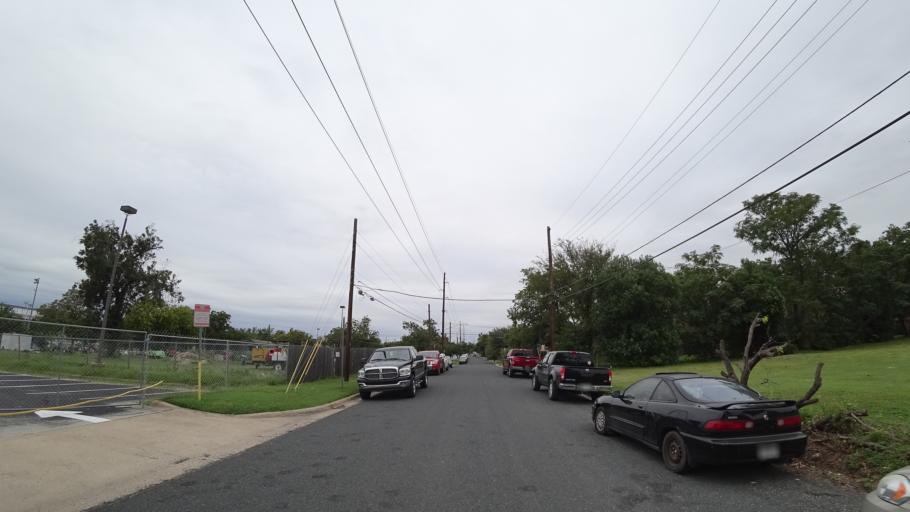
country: US
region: Texas
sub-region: Travis County
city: Austin
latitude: 30.2808
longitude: -97.7235
